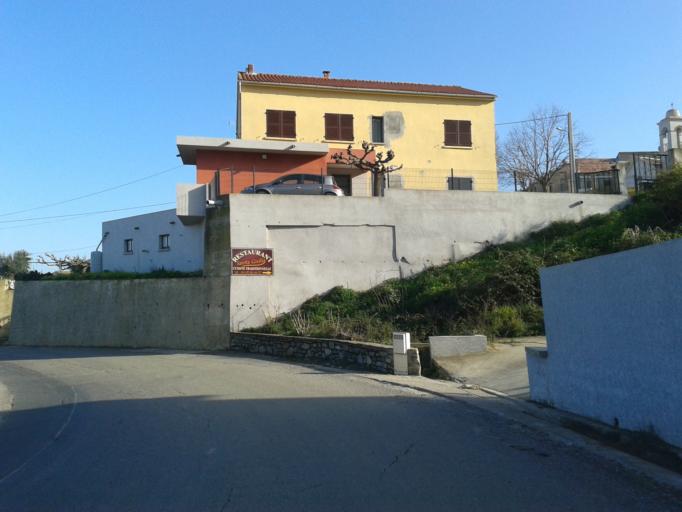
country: FR
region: Corsica
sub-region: Departement de la Haute-Corse
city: Biguglia
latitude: 42.5941
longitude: 9.4262
